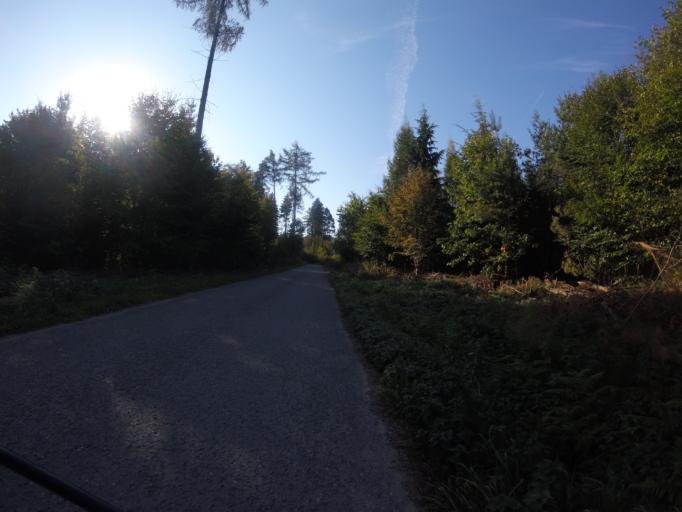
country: DE
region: Baden-Wuerttemberg
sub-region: Regierungsbezirk Stuttgart
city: Oppenweiler
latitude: 48.9998
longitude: 9.4285
